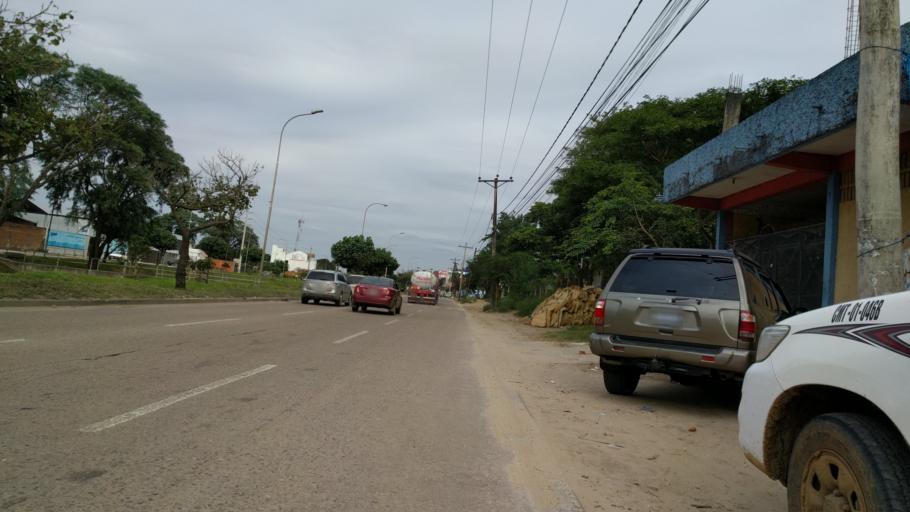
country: BO
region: Santa Cruz
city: Santa Cruz de la Sierra
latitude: -17.8027
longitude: -63.2146
